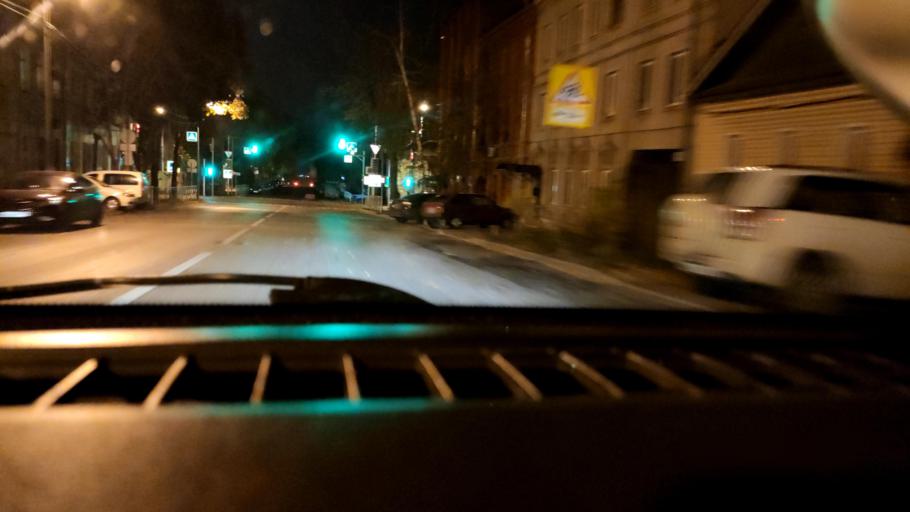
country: RU
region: Samara
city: Rozhdestveno
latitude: 53.1813
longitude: 50.0836
